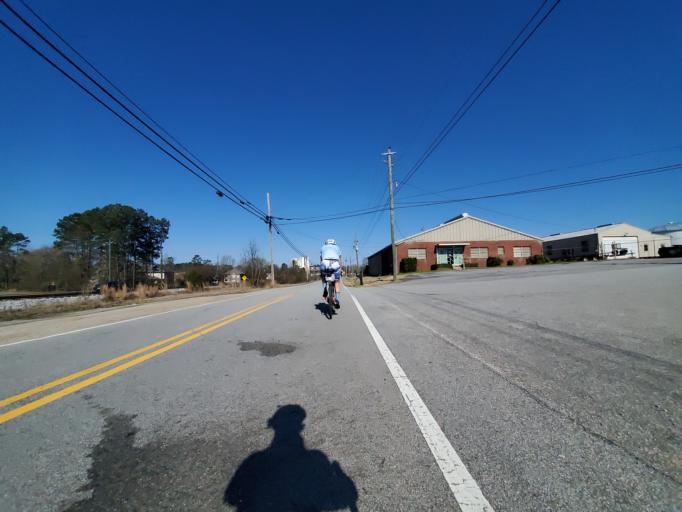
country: US
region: Georgia
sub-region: Clarke County
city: Country Club Estates
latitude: 33.9867
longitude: -83.4204
